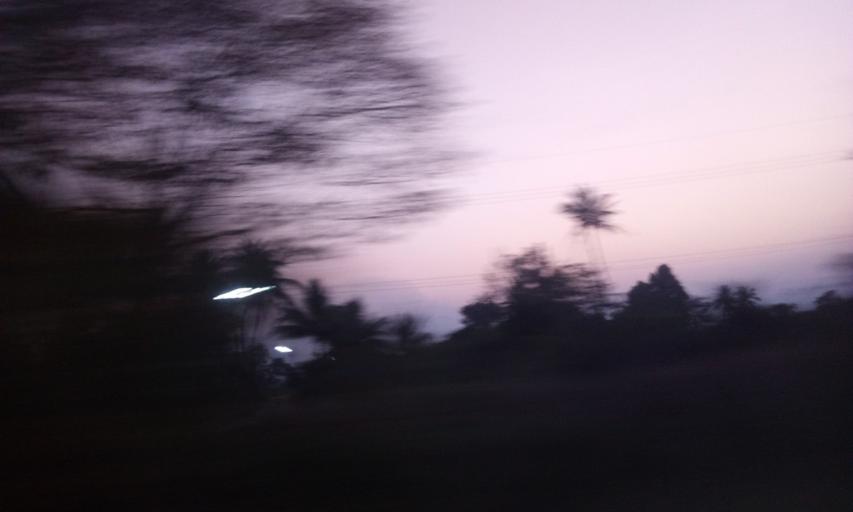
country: TH
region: Sing Buri
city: Sing Buri
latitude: 14.8362
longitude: 100.3968
